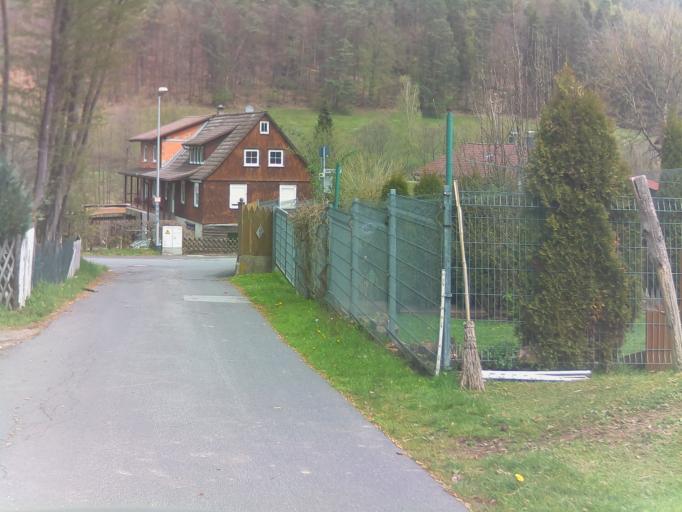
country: DE
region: Hesse
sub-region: Regierungsbezirk Darmstadt
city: Wald-Michelbach
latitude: 49.6374
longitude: 8.8994
